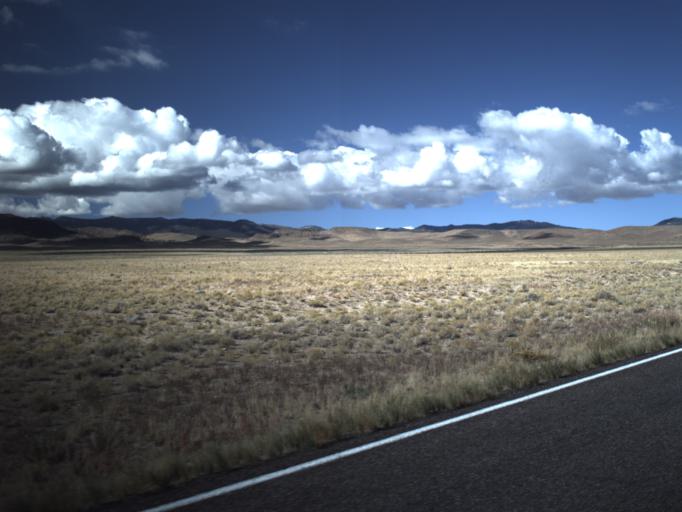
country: US
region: Utah
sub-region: Beaver County
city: Milford
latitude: 38.5744
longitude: -113.7958
